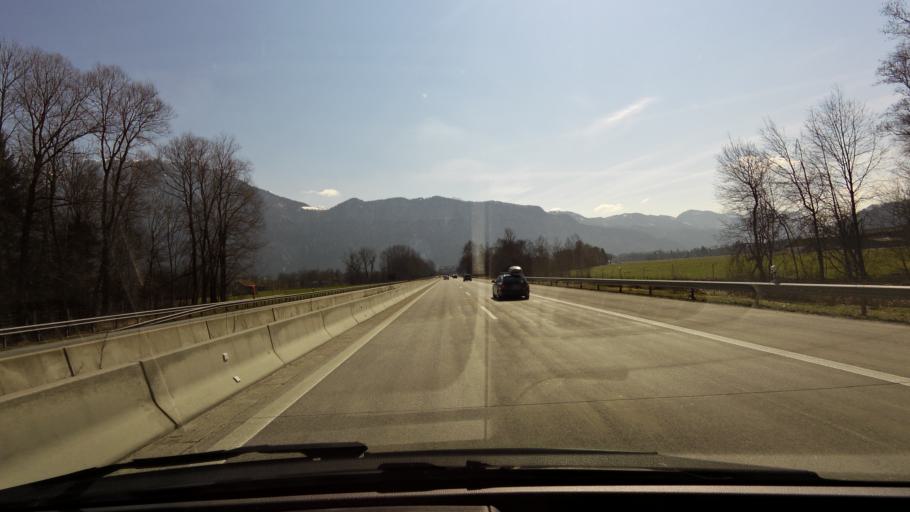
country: AT
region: Tyrol
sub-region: Politischer Bezirk Kufstein
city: Ebbs
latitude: 47.6366
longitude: 12.1954
